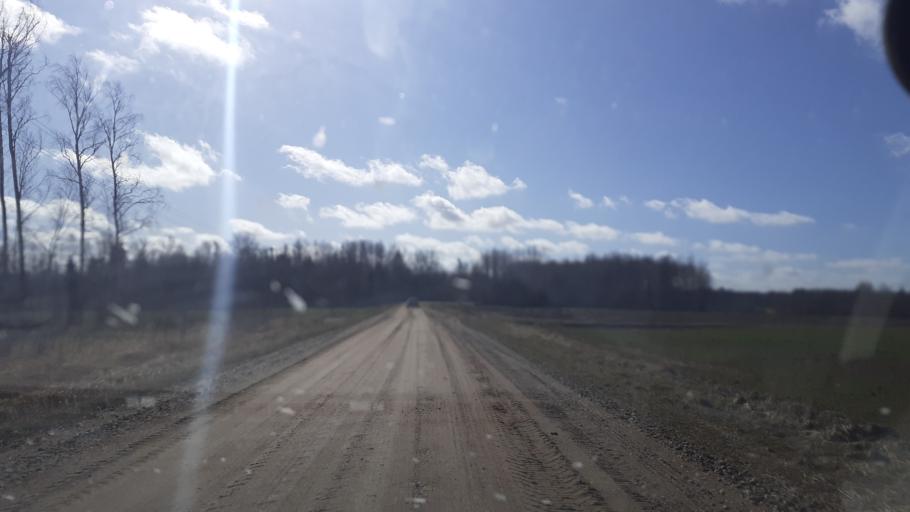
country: LV
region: Kuldigas Rajons
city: Kuldiga
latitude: 56.9159
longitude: 22.1265
